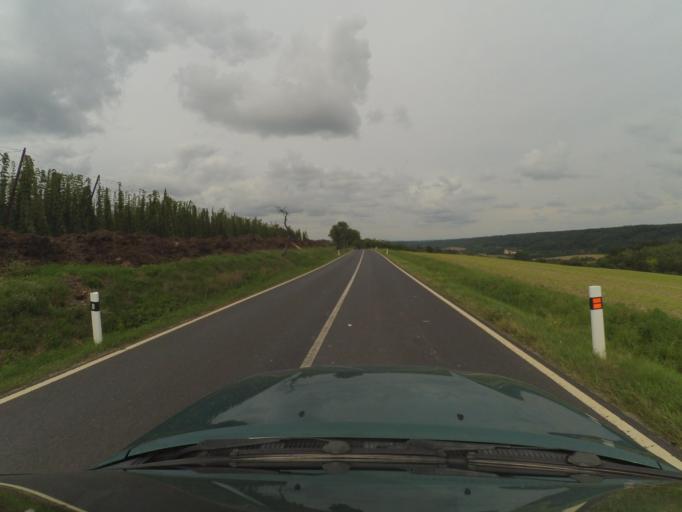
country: CZ
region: Central Bohemia
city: Revnicov
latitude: 50.2424
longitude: 13.7606
